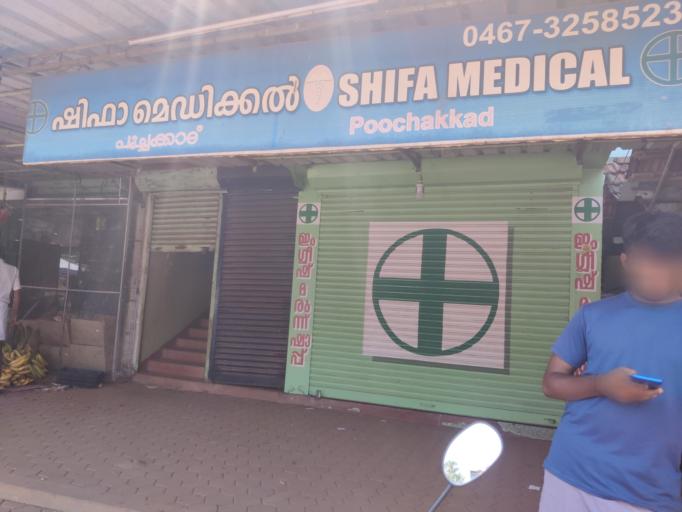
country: IN
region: Kerala
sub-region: Kasaragod District
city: Kannangad
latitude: 12.3789
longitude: 75.0515
